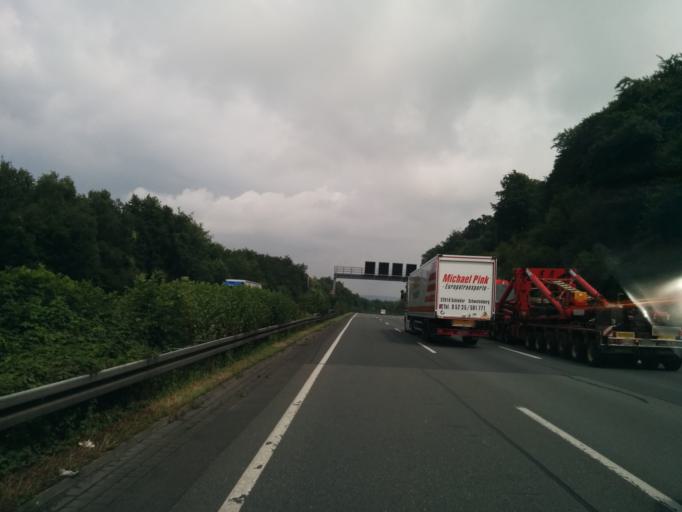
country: DE
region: Lower Saxony
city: Luhden
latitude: 52.2193
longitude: 9.0579
